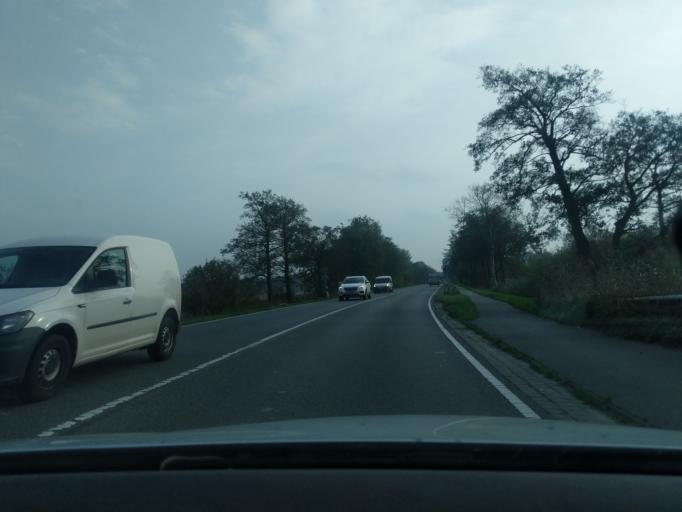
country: DE
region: Lower Saxony
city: Burweg
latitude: 53.6363
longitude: 9.2576
